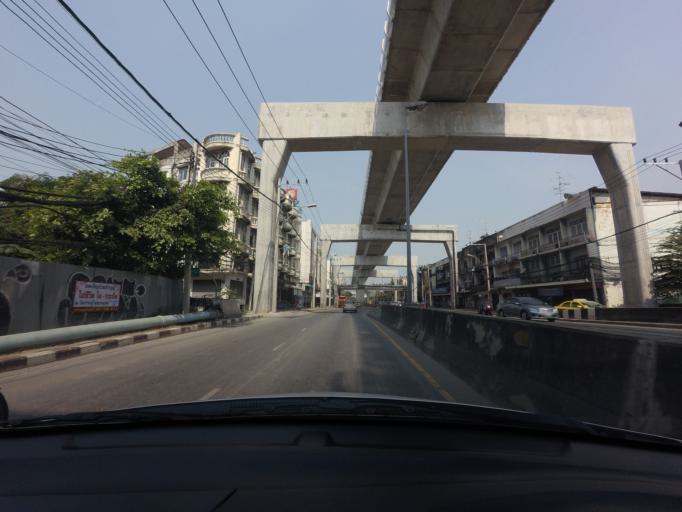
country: TH
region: Bangkok
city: Bangkok Yai
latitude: 13.7326
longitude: 100.4724
